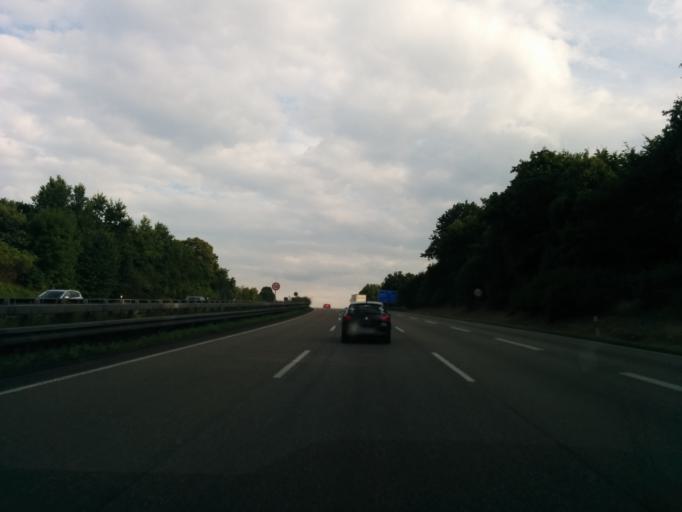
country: DE
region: Hesse
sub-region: Regierungsbezirk Kassel
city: Guxhagen
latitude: 51.1998
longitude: 9.4669
